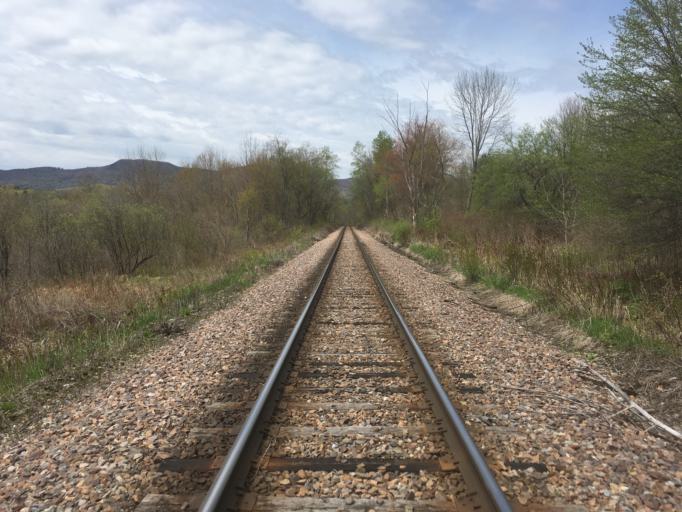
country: US
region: Vermont
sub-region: Rutland County
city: Brandon
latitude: 43.7151
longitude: -73.0453
